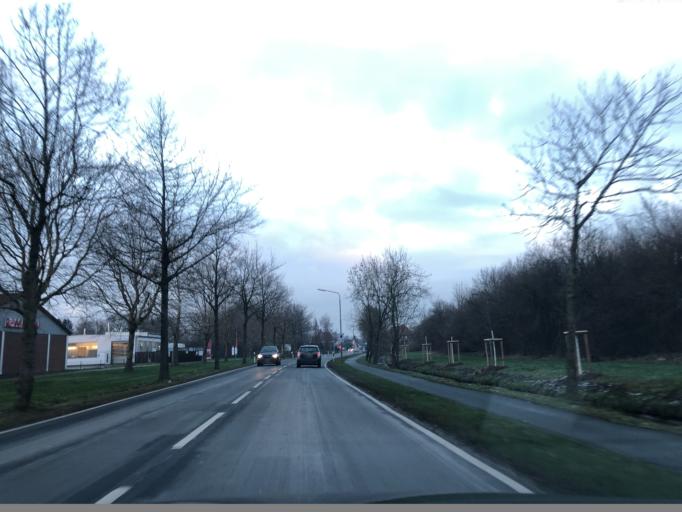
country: DE
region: Lower Saxony
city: Lemwerder
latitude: 53.1559
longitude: 8.6092
